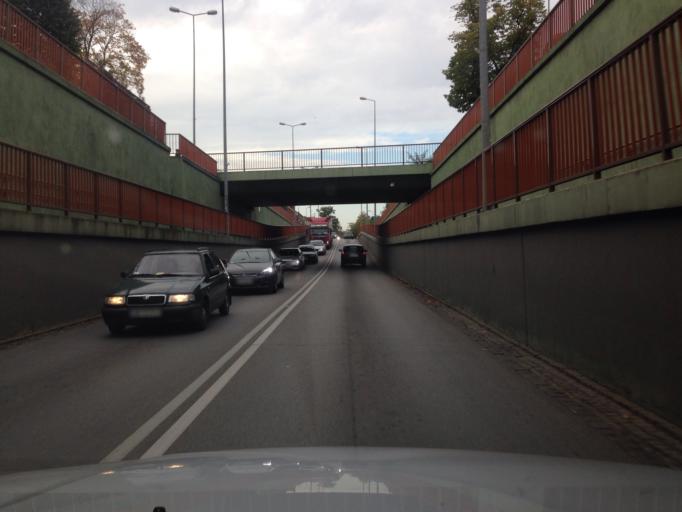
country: PL
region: Pomeranian Voivodeship
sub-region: Powiat leborski
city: Lebork
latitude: 54.5353
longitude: 17.7544
